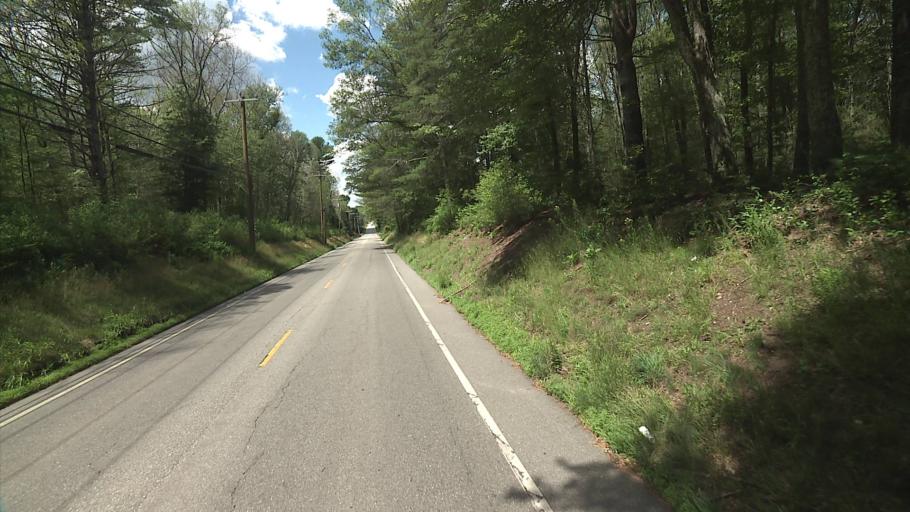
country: US
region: Rhode Island
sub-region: Washington County
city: Ashaway
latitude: 41.4356
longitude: -71.8223
